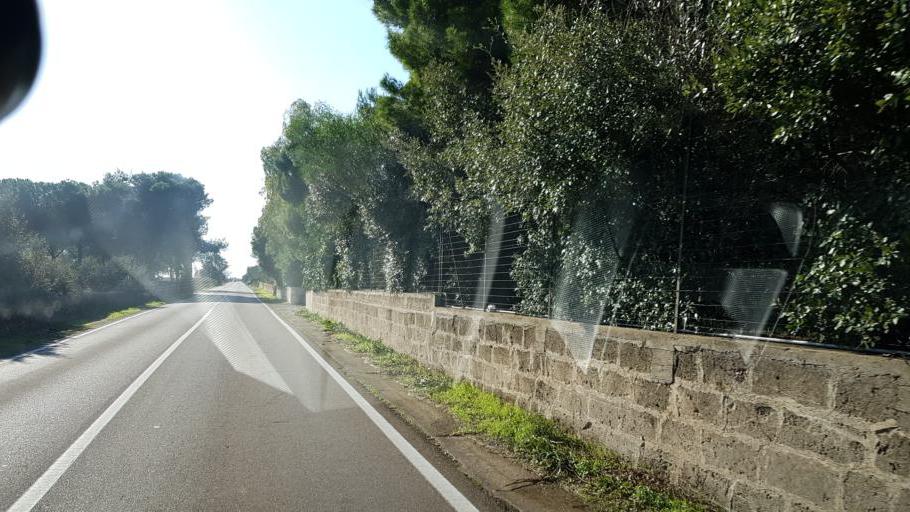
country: IT
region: Apulia
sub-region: Provincia di Lecce
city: Trepuzzi
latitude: 40.4521
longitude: 18.1107
